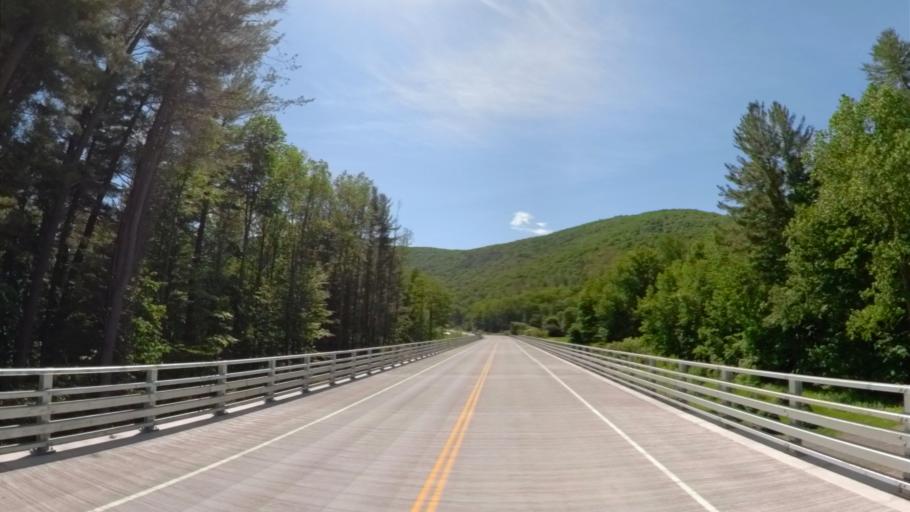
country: US
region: New York
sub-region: Ulster County
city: Shokan
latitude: 42.1047
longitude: -74.4468
